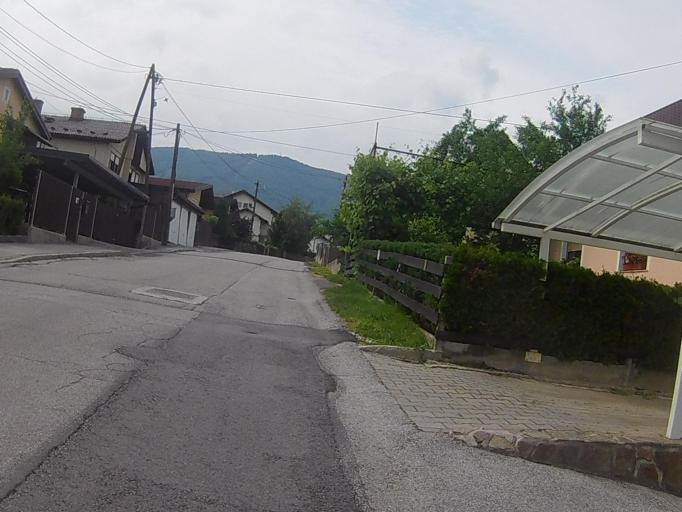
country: SI
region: Maribor
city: Pekre
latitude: 46.5459
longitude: 15.5957
